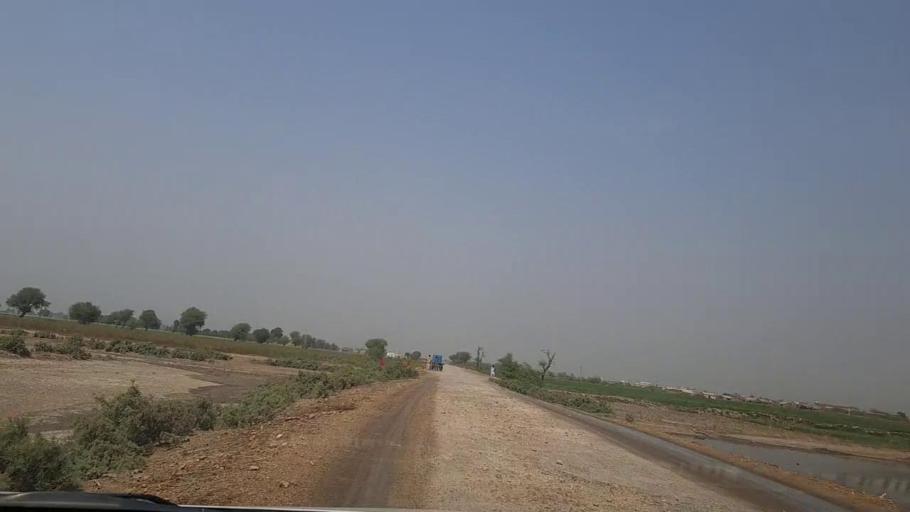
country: PK
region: Sindh
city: Pithoro
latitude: 25.5531
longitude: 69.2275
